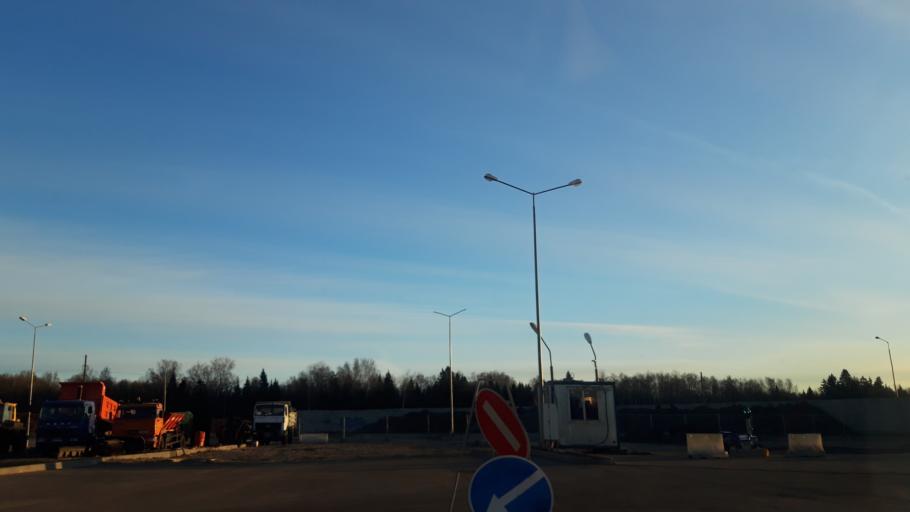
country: RU
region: Moskovskaya
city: Rzhavki
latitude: 55.9972
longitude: 37.2636
